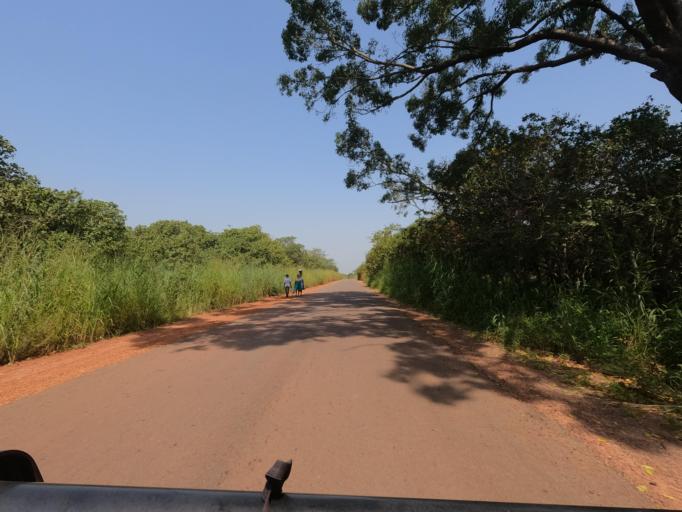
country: SN
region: Ziguinchor
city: Adeane
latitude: 12.3852
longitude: -15.7811
